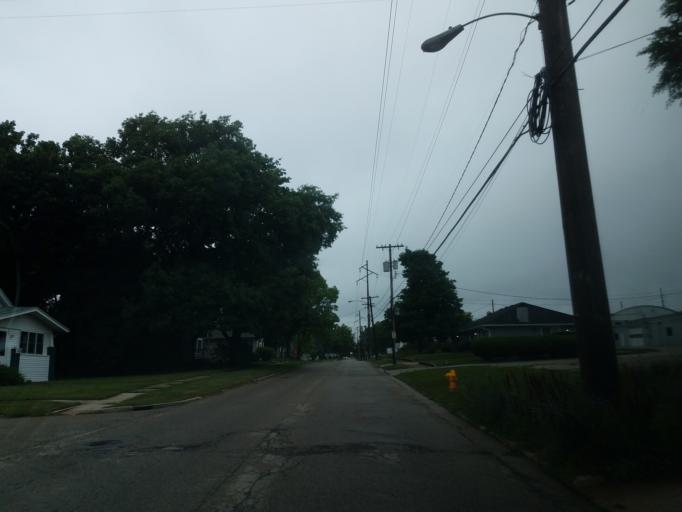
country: US
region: Illinois
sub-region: McLean County
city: Bloomington
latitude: 40.4681
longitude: -88.9817
